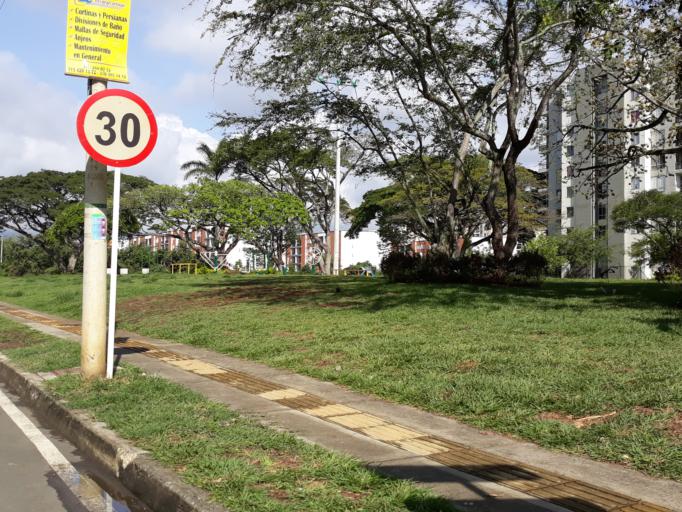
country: CO
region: Valle del Cauca
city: Cali
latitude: 3.3569
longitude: -76.5150
